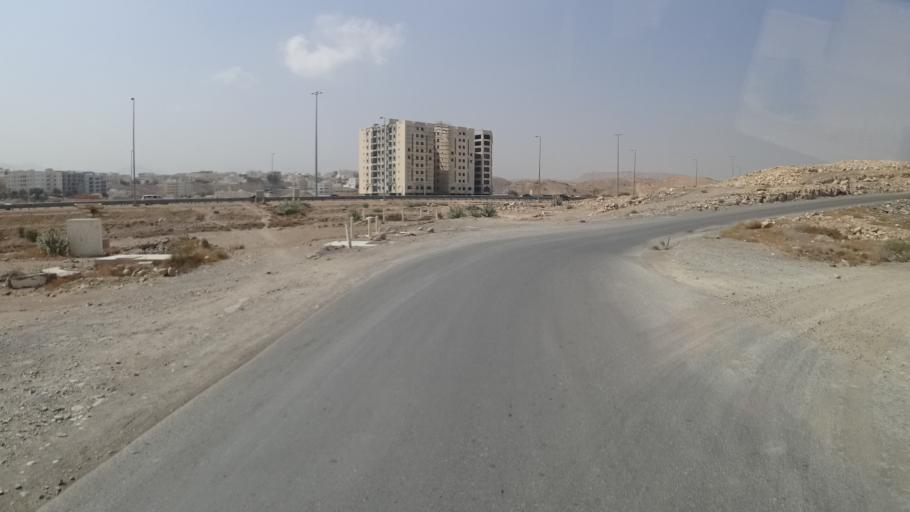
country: OM
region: Muhafazat Masqat
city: Bawshar
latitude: 23.5639
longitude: 58.3464
